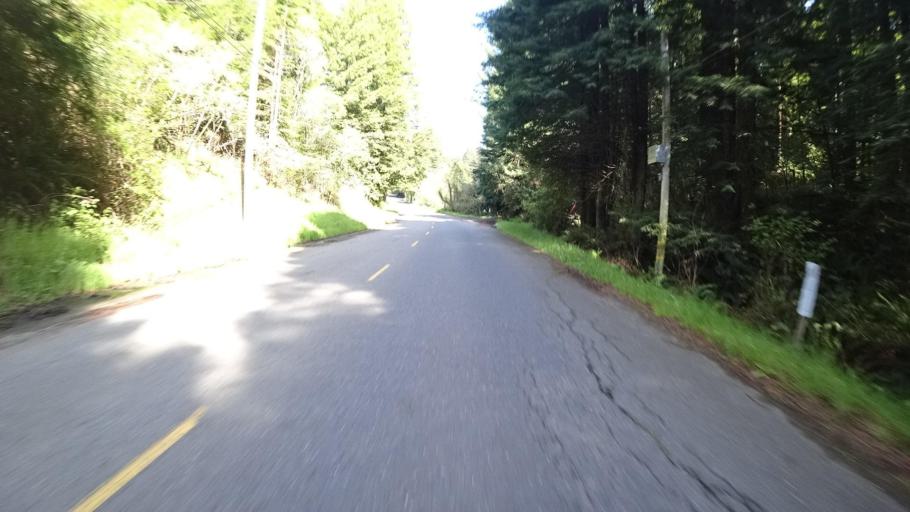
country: US
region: California
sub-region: Humboldt County
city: Hydesville
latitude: 40.5687
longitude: -124.1167
